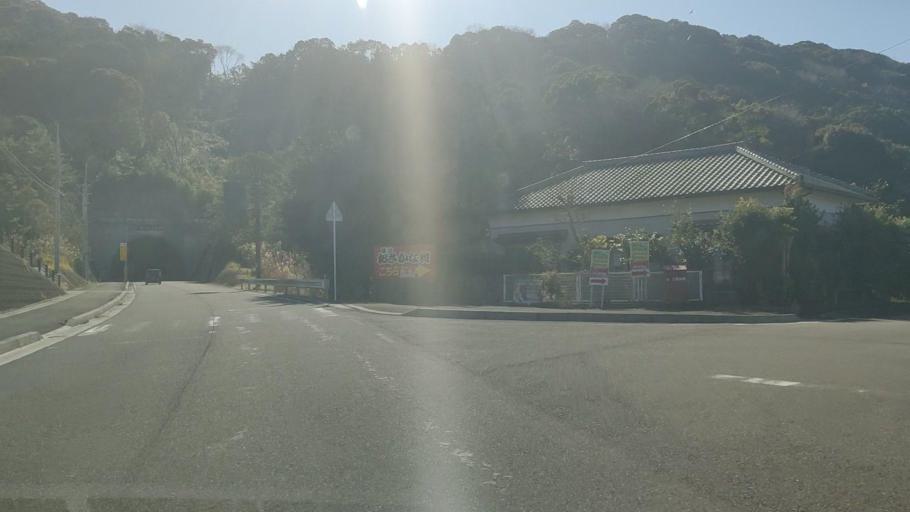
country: JP
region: Oita
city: Saiki
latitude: 32.7988
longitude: 131.9004
